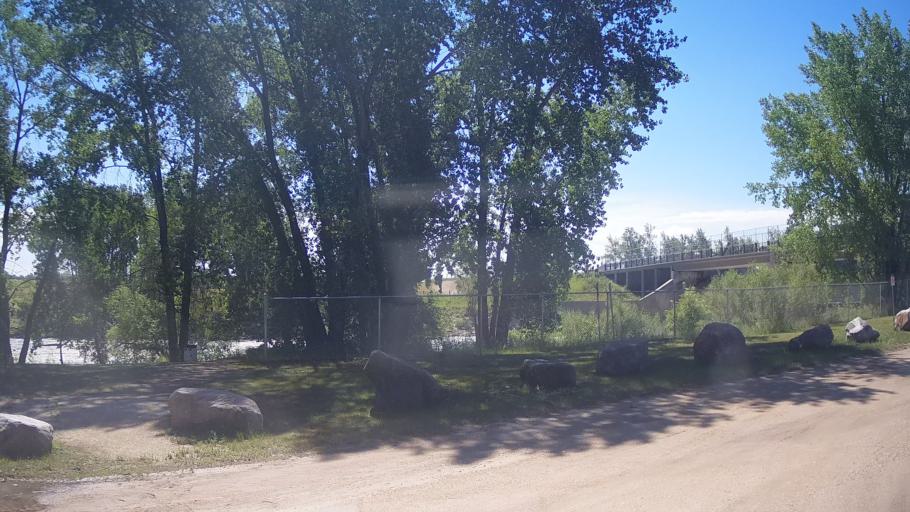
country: CA
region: Manitoba
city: Portage la Prairie
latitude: 49.9478
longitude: -98.3299
